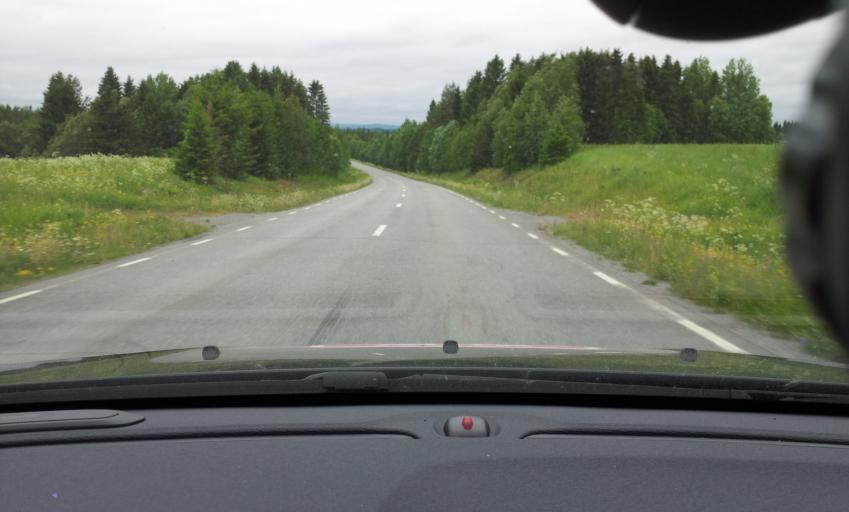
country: SE
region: Jaemtland
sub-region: Bergs Kommun
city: Hoverberg
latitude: 63.0011
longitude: 14.3823
